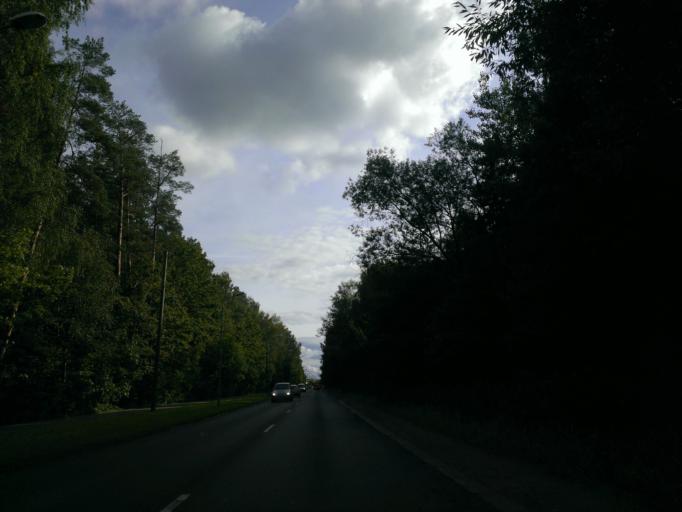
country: LV
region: Stopini
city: Ulbroka
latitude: 56.9658
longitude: 24.2525
